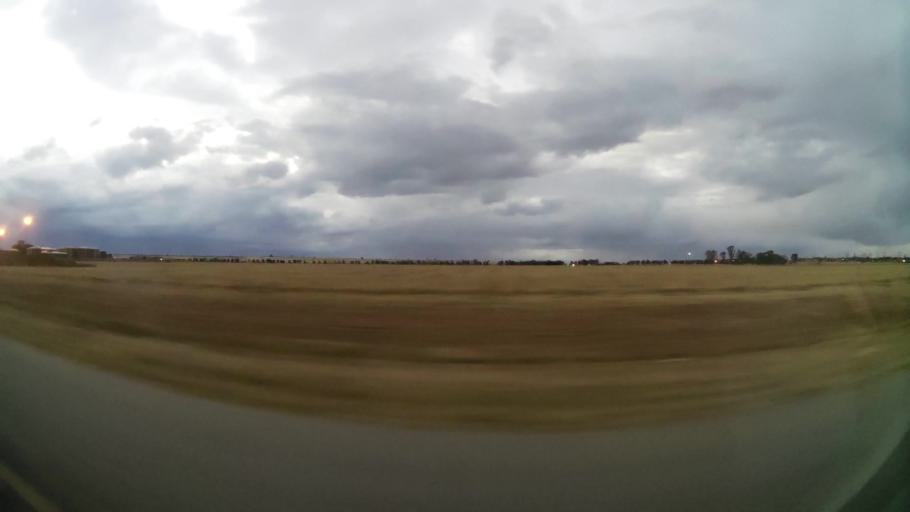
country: ZA
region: Orange Free State
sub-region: Lejweleputswa District Municipality
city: Welkom
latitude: -27.9504
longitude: 26.7939
